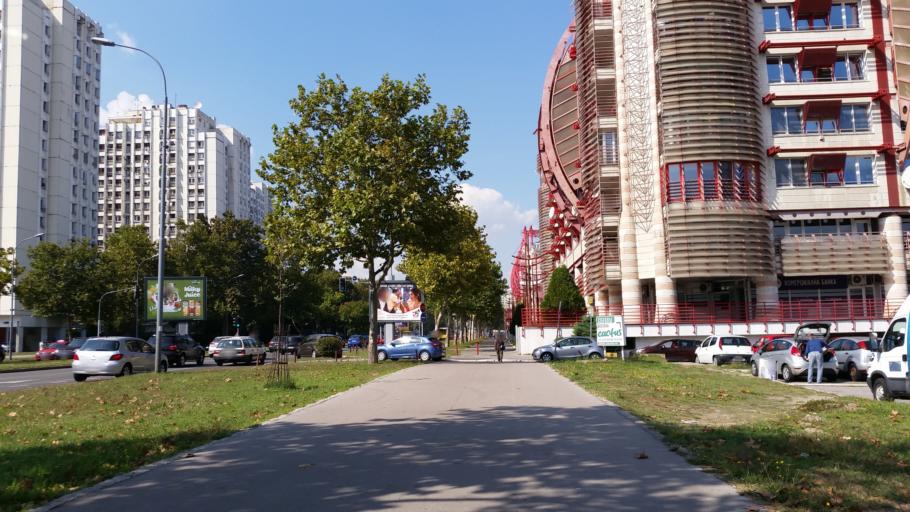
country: RS
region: Central Serbia
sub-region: Belgrade
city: Novi Beograd
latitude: 44.8211
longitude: 20.4209
